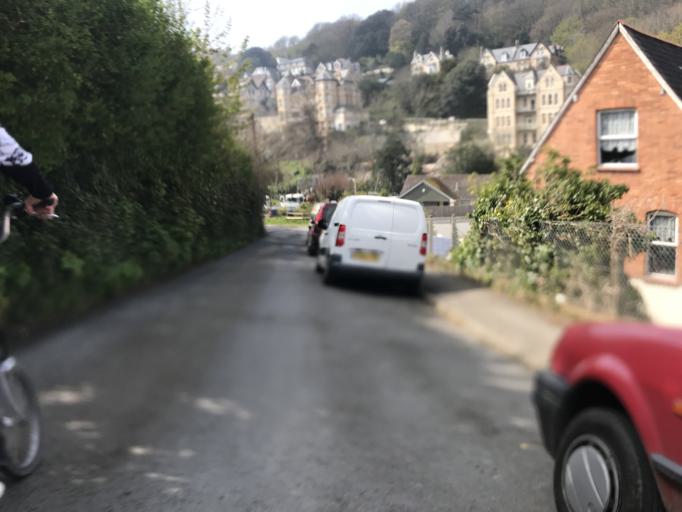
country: GB
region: England
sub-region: Devon
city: Ilfracombe
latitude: 51.2062
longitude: -4.1293
